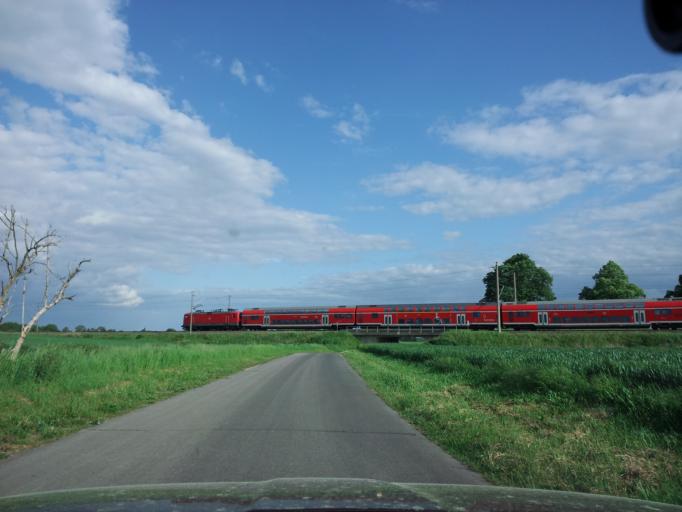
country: DE
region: Saxony-Anhalt
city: Seyda
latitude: 51.9571
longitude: 12.8995
